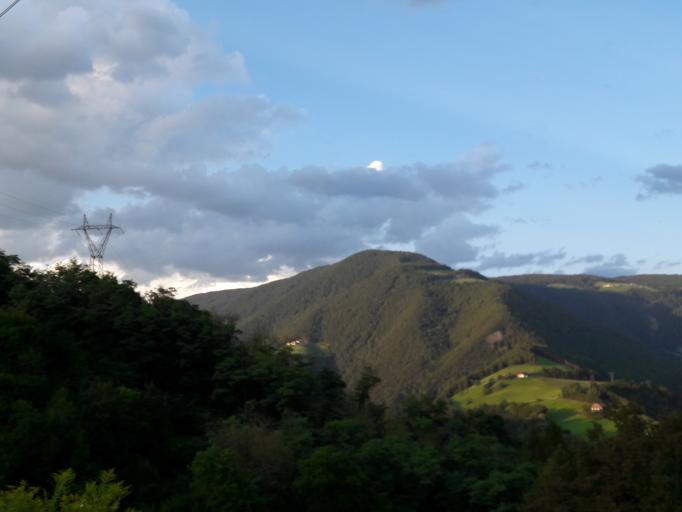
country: IT
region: Trentino-Alto Adige
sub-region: Bolzano
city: Sciaves
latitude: 46.7497
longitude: 11.6850
